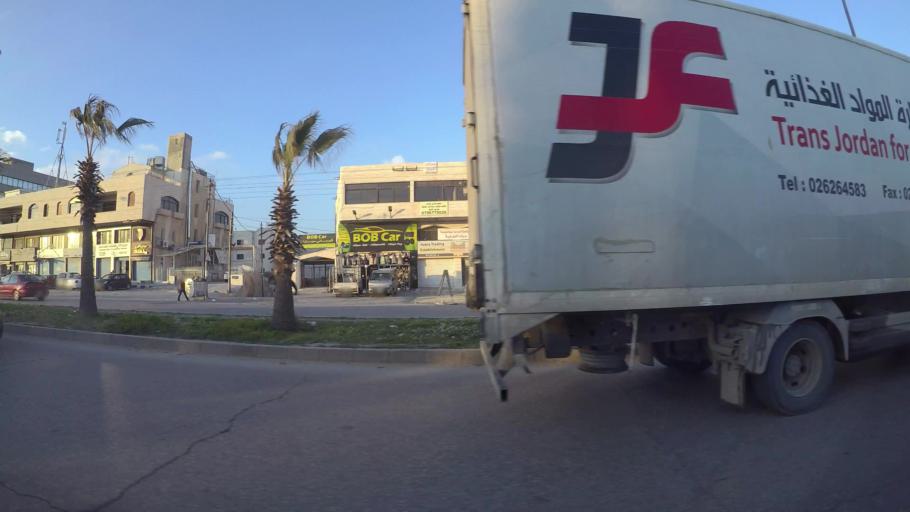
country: JO
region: Amman
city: Al Quwaysimah
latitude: 31.9071
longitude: 35.9316
